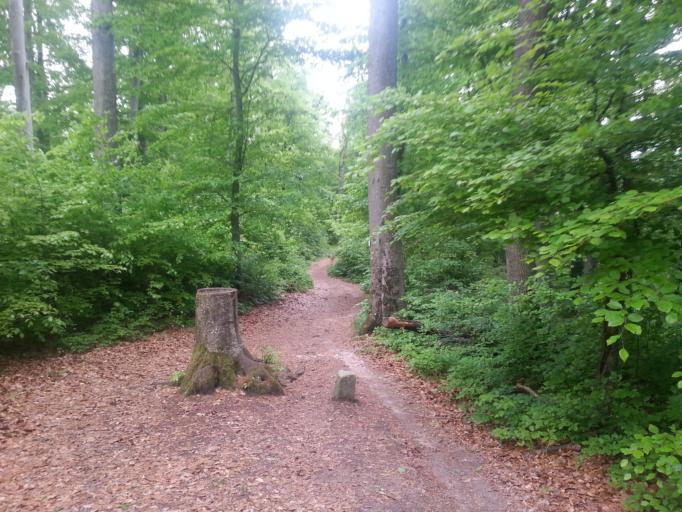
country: DE
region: Baden-Wuerttemberg
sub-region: Regierungsbezirk Stuttgart
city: Hildrizhausen
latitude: 48.5817
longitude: 8.9318
